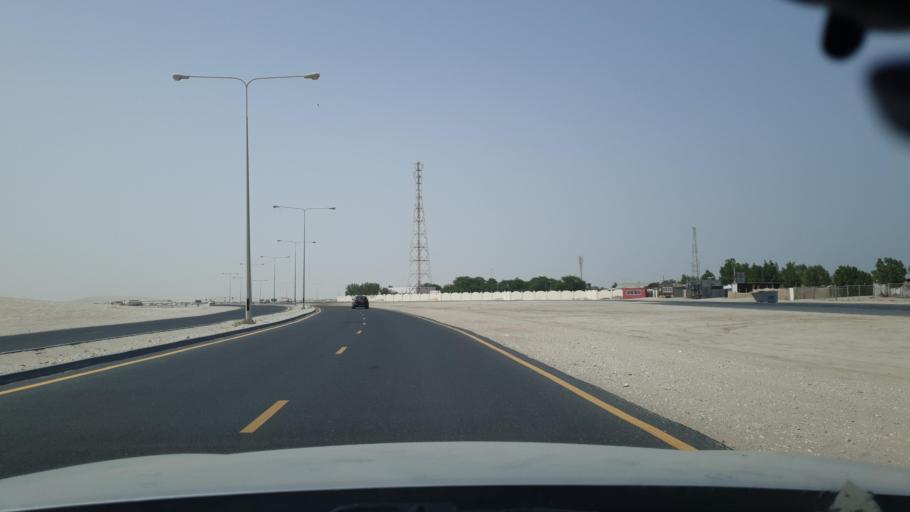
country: QA
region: Al Wakrah
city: Umm Sa'id
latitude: 24.8563
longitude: 51.5107
